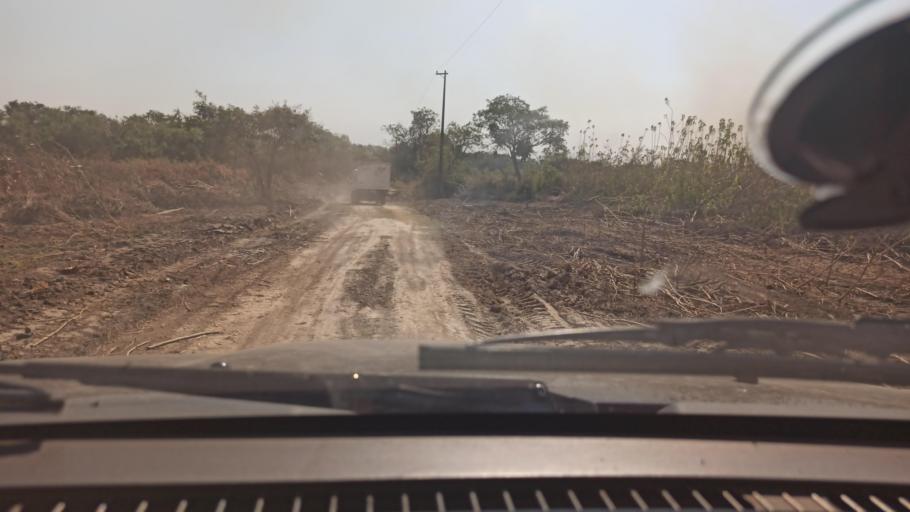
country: PY
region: Asuncion
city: Asuncion
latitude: -25.3412
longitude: -57.6773
